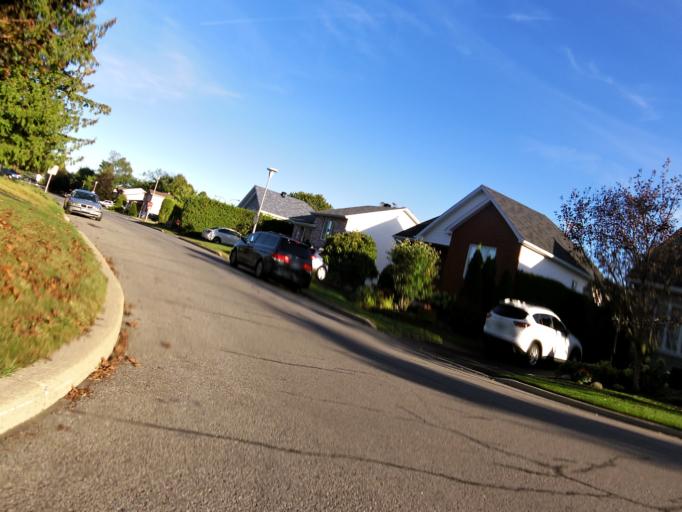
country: CA
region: Ontario
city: Bells Corners
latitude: 45.4178
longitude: -75.8459
